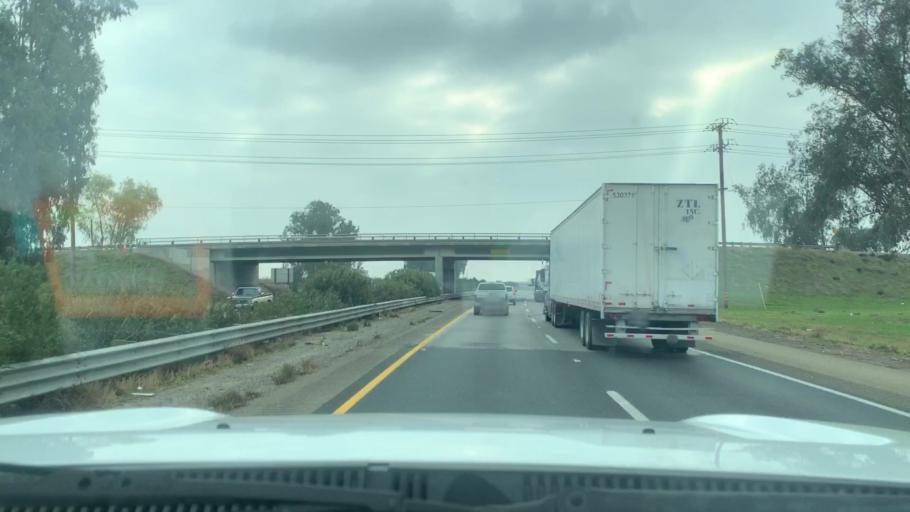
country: US
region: California
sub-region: Tulare County
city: Tipton
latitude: 36.0520
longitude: -119.3110
